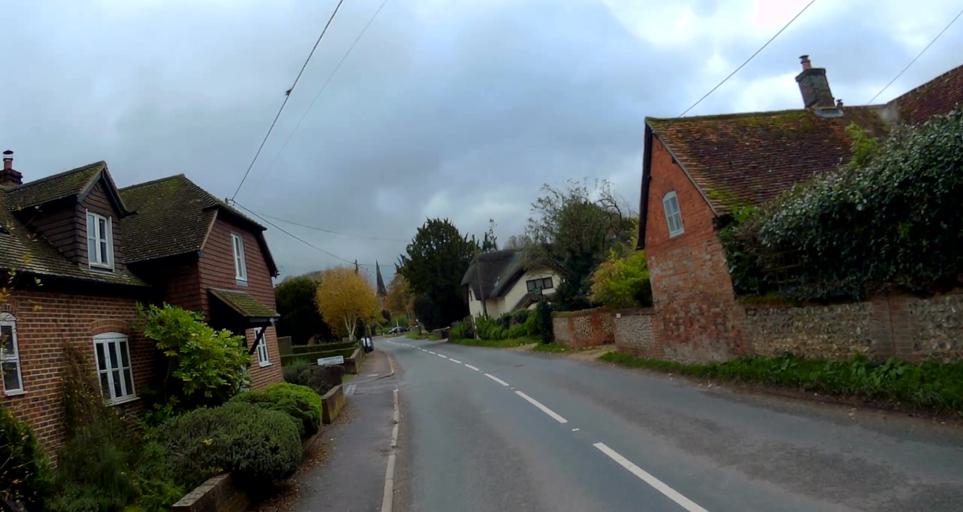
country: GB
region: England
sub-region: Hampshire
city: Basingstoke
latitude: 51.1721
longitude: -1.1331
